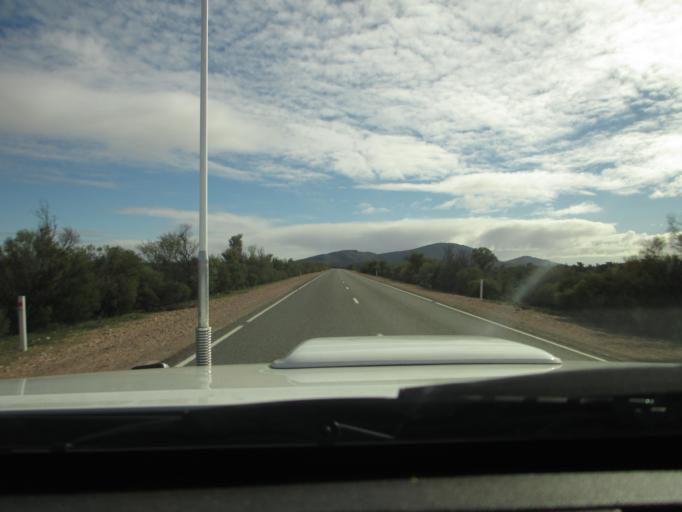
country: AU
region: South Australia
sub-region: Flinders Ranges
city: Quorn
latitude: -31.8291
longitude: 138.3843
